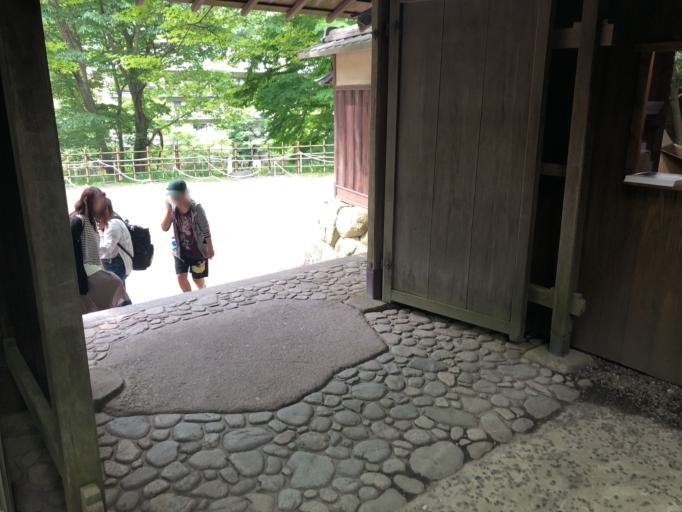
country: JP
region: Kyoto
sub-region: Kyoto-shi
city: Kamigyo-ku
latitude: 35.0638
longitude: 135.8086
